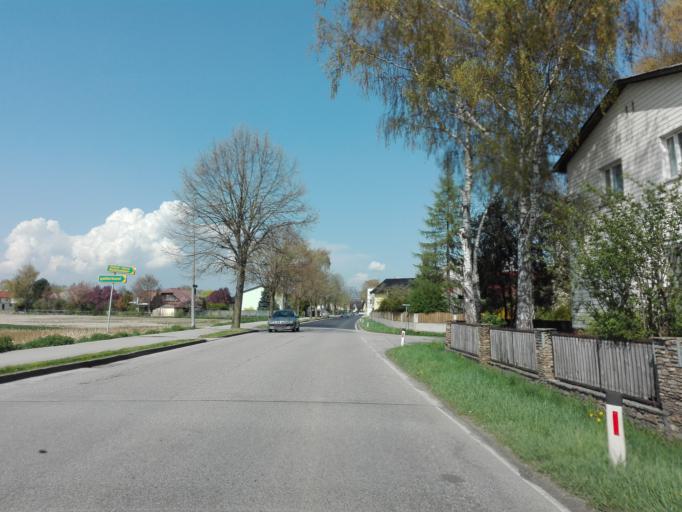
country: AT
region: Upper Austria
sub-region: Politischer Bezirk Linz-Land
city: Traun
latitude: 48.2307
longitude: 14.2652
